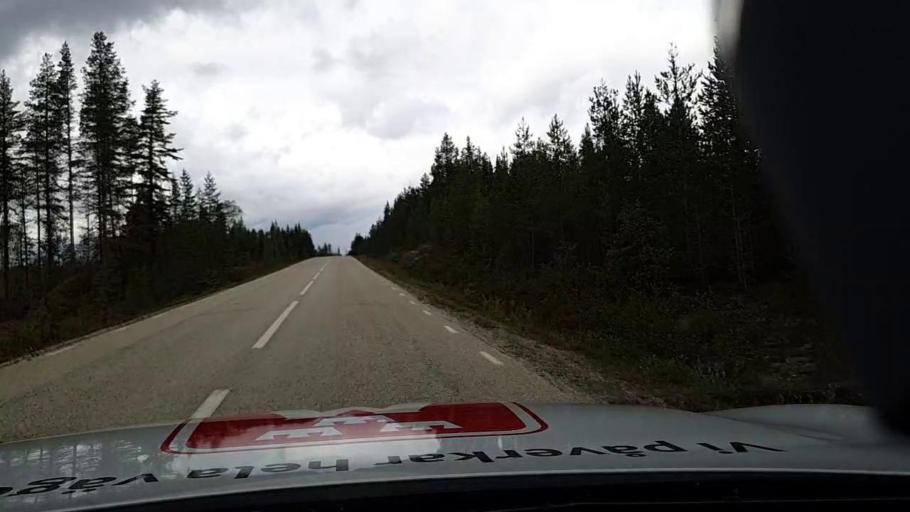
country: SE
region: Jaemtland
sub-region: Are Kommun
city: Jarpen
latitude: 62.7617
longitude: 13.7315
